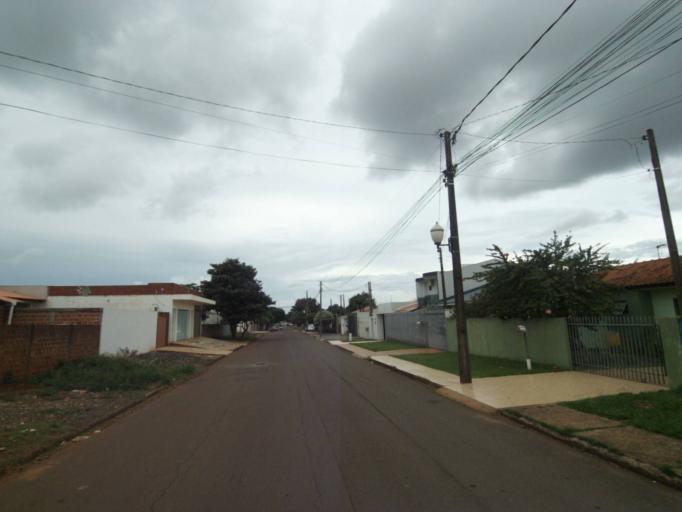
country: BR
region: Parana
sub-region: Campo Mourao
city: Campo Mourao
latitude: -24.0261
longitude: -52.3601
